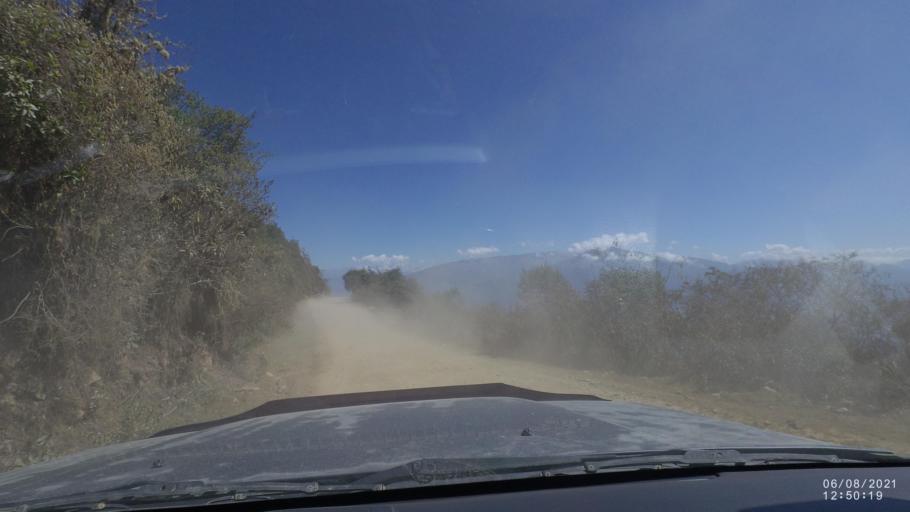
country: BO
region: Cochabamba
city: Colchani
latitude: -16.7598
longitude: -66.6767
